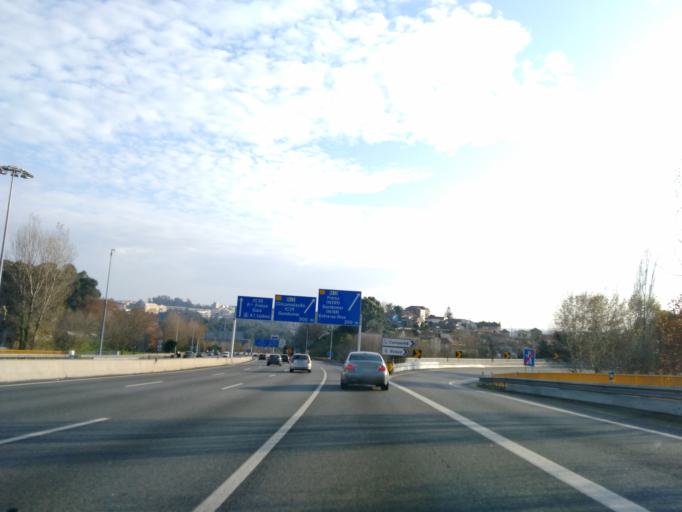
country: PT
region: Porto
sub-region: Gondomar
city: Valbom
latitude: 41.1539
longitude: -8.5824
